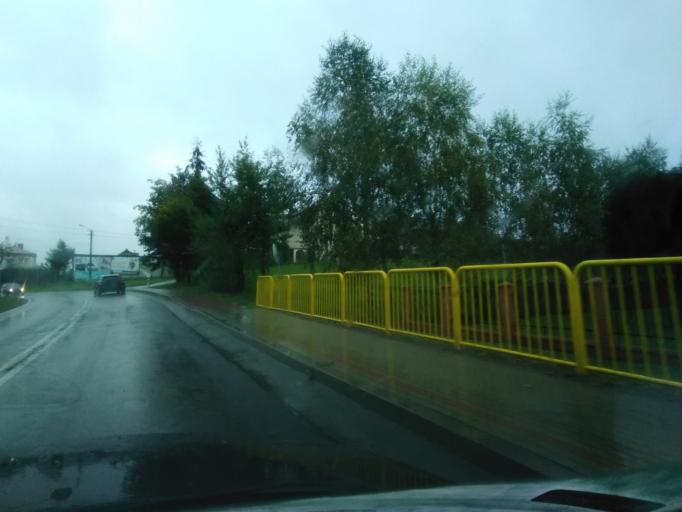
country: PL
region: Subcarpathian Voivodeship
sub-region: Powiat ropczycko-sedziszowski
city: Wielopole Skrzynskie
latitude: 49.9746
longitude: 21.5749
